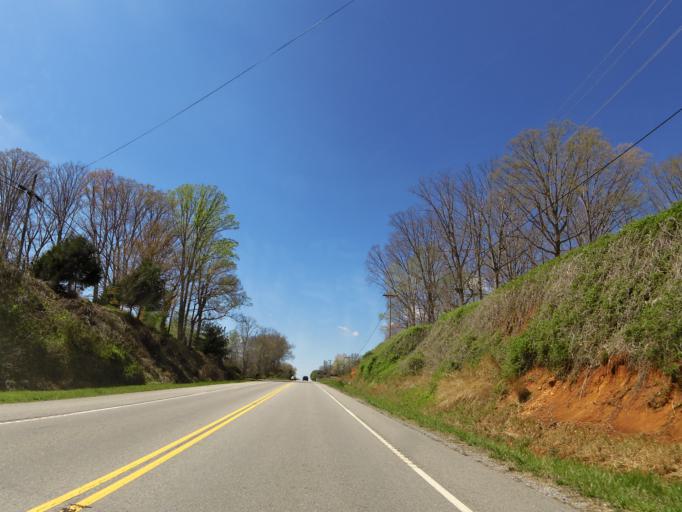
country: US
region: Tennessee
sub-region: White County
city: Sparta
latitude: 35.9558
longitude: -85.5815
